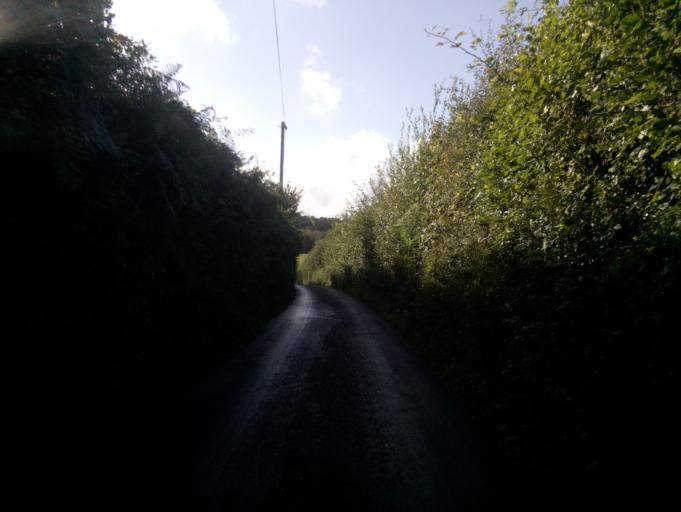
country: GB
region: England
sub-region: Devon
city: Totnes
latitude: 50.3473
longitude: -3.7029
